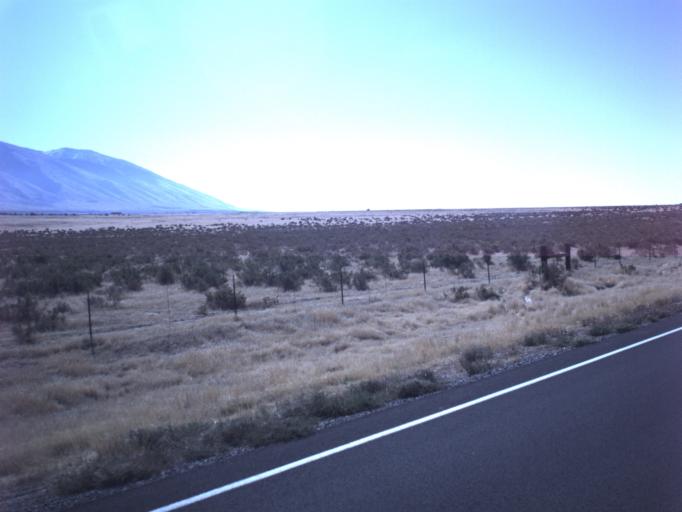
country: US
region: Utah
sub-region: Tooele County
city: Grantsville
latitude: 40.5476
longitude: -112.7420
